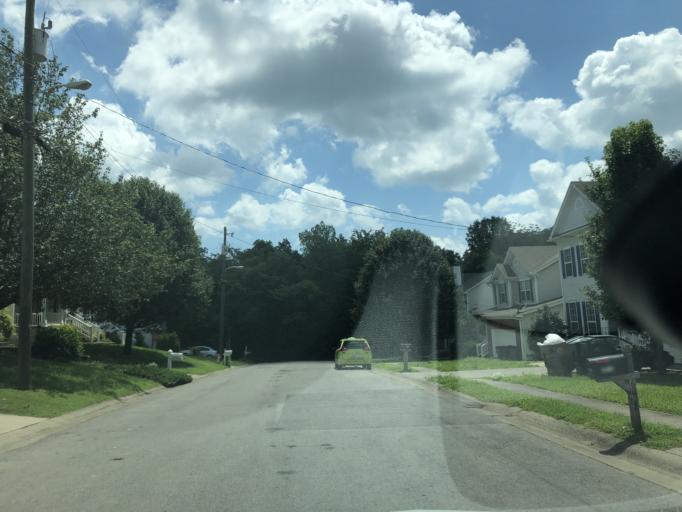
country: US
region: Tennessee
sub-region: Rutherford County
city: La Vergne
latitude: 36.0398
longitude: -86.6244
